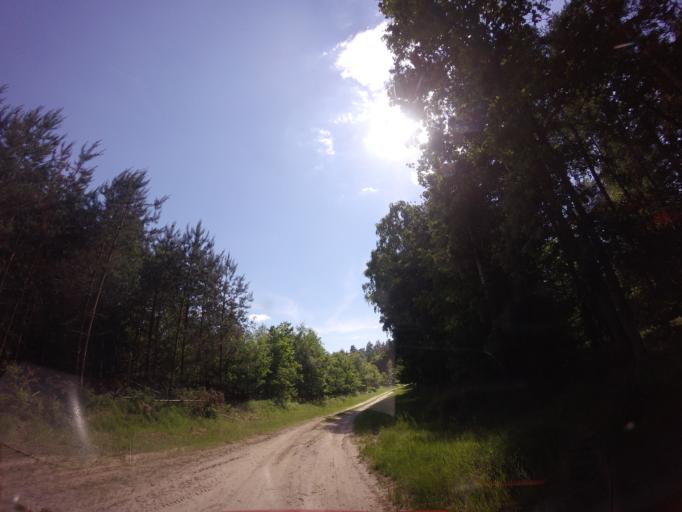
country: PL
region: West Pomeranian Voivodeship
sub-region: Powiat choszczenski
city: Drawno
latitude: 53.1683
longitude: 15.6476
